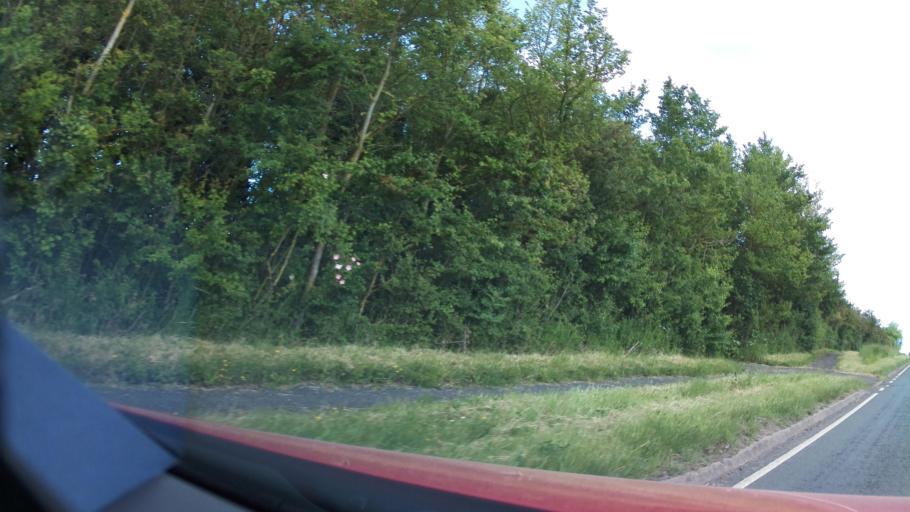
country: GB
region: England
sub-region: Worcestershire
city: Kempsey
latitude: 52.1550
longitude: -2.1531
